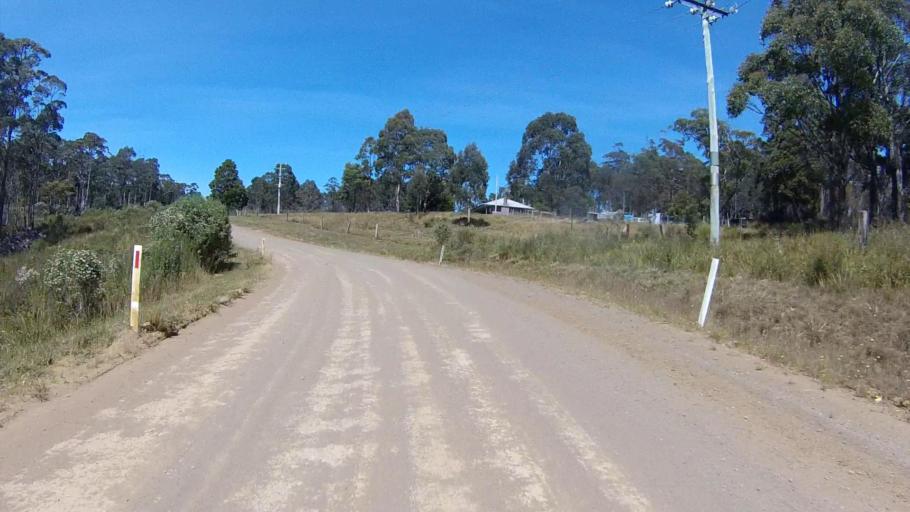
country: AU
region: Tasmania
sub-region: Sorell
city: Sorell
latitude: -42.7291
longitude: 147.7394
